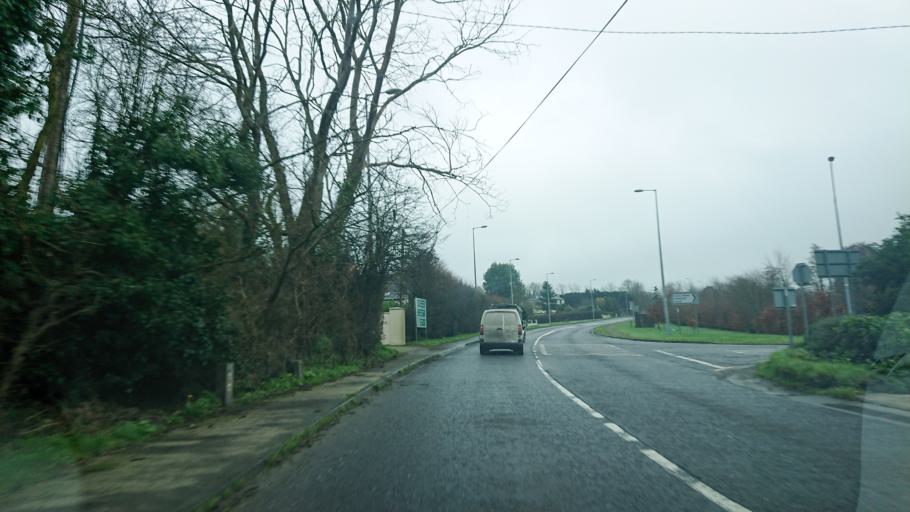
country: IE
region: Munster
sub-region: County Cork
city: Bandon
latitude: 51.7659
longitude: -8.6522
